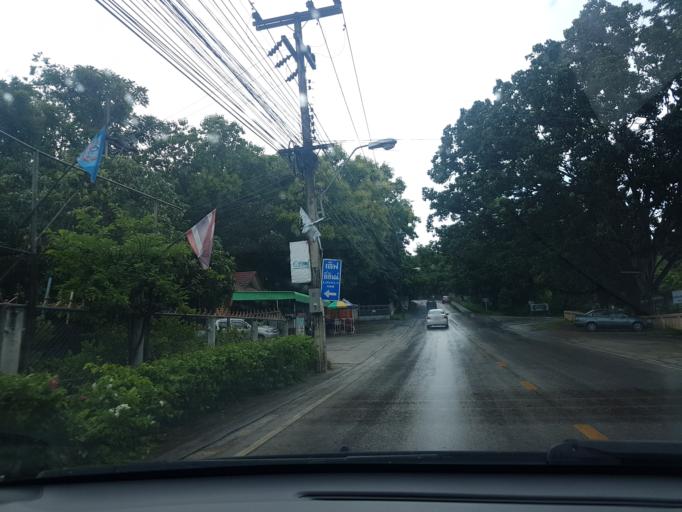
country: TH
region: Lampang
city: Lampang
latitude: 18.2972
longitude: 99.4713
